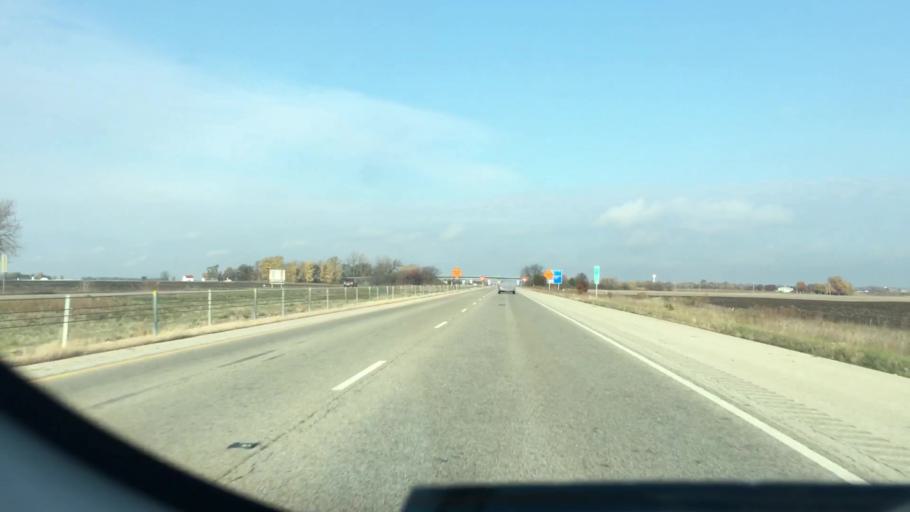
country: US
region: Illinois
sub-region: McLean County
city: Danvers
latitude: 40.5621
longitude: -89.1129
